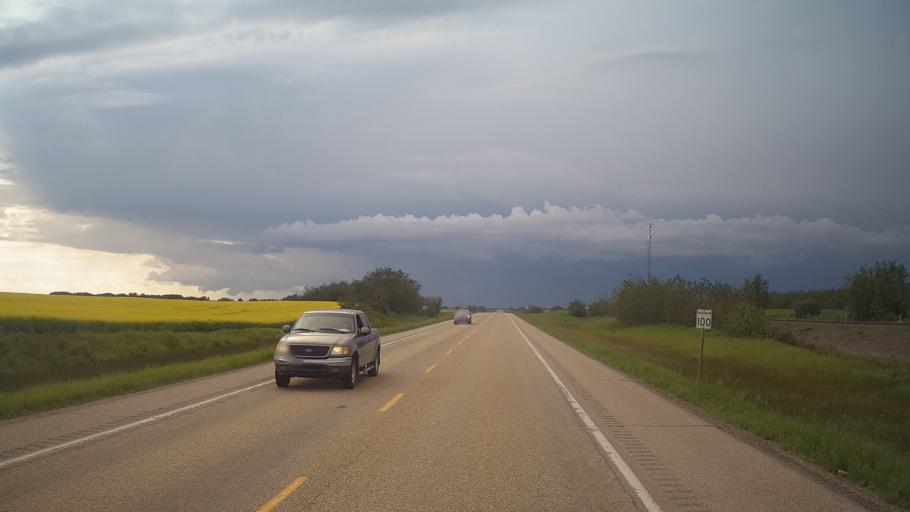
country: CA
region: Alberta
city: Vegreville
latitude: 53.2355
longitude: -112.2542
